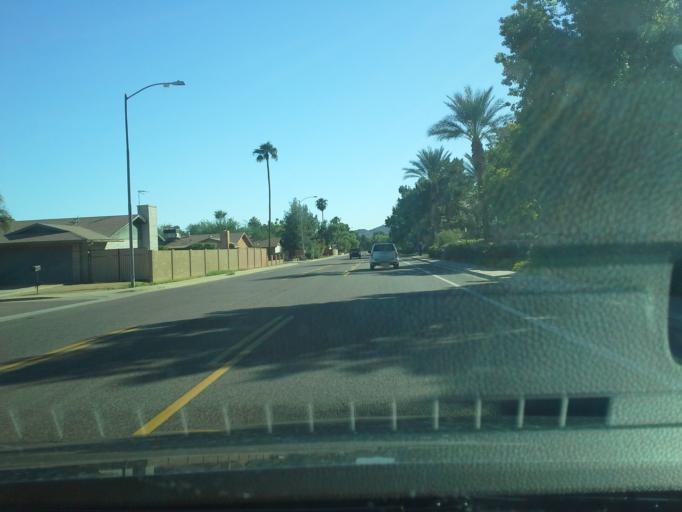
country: US
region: Arizona
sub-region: Maricopa County
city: Paradise Valley
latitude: 33.6091
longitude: -111.9866
